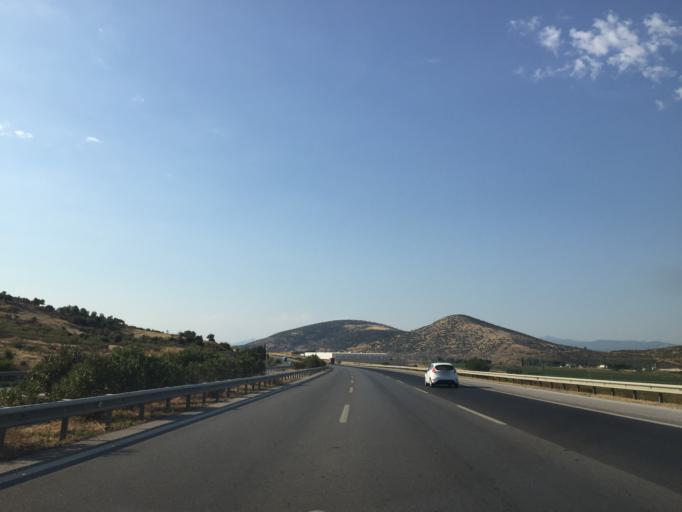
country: TR
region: Izmir
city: Belevi
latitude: 38.0447
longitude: 27.4287
